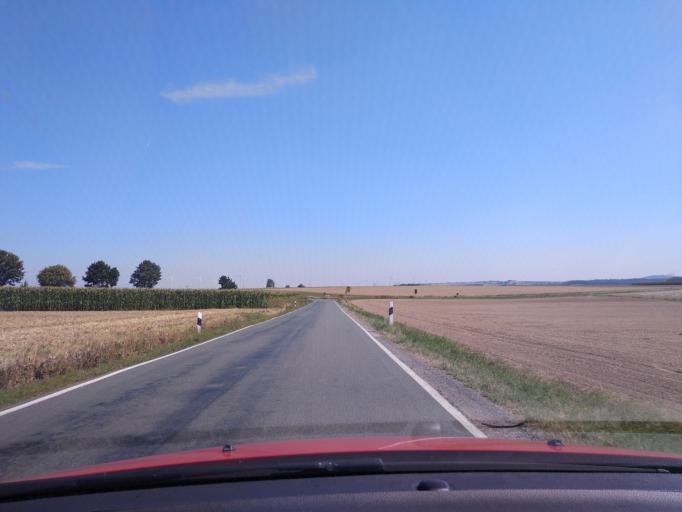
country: DE
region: North Rhine-Westphalia
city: Borgentreich
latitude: 51.6452
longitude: 9.2502
